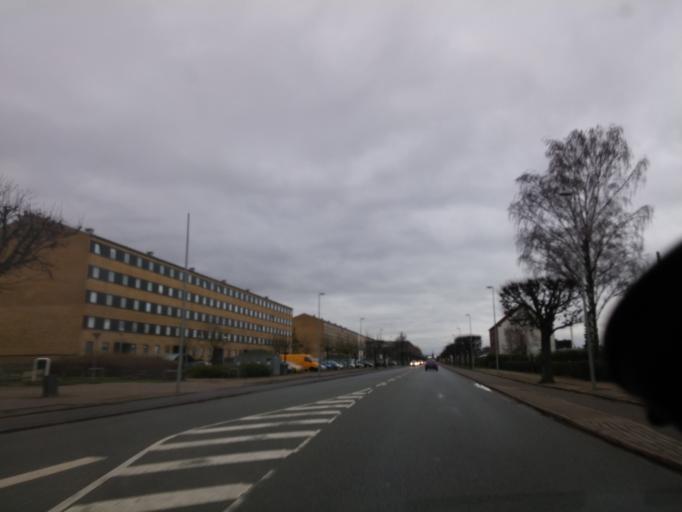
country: DK
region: South Denmark
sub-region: Odense Kommune
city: Neder Holluf
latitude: 55.3924
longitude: 10.4311
